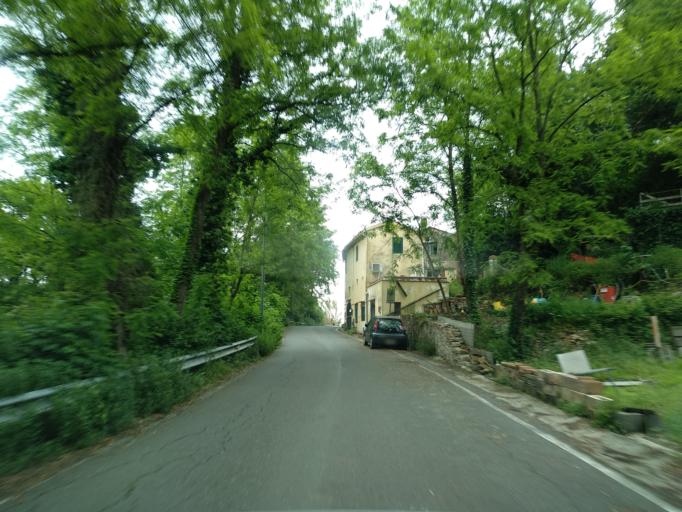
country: IT
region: Tuscany
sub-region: Provincia di Livorno
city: Guasticce
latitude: 43.5434
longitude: 10.4358
